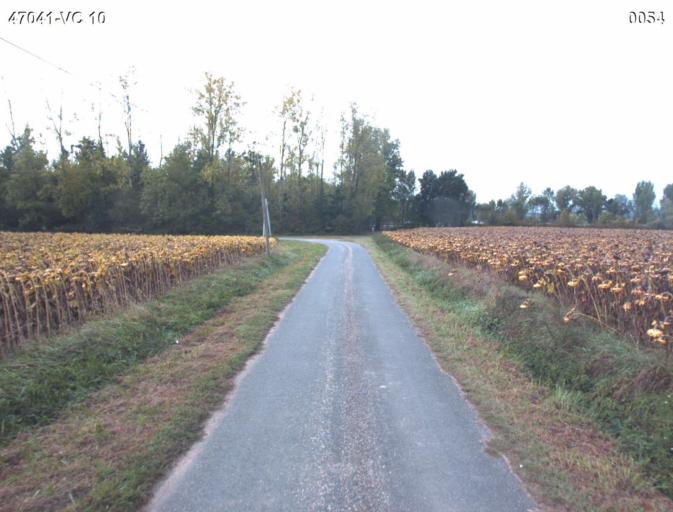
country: FR
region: Aquitaine
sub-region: Departement du Lot-et-Garonne
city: Port-Sainte-Marie
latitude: 44.2140
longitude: 0.4290
